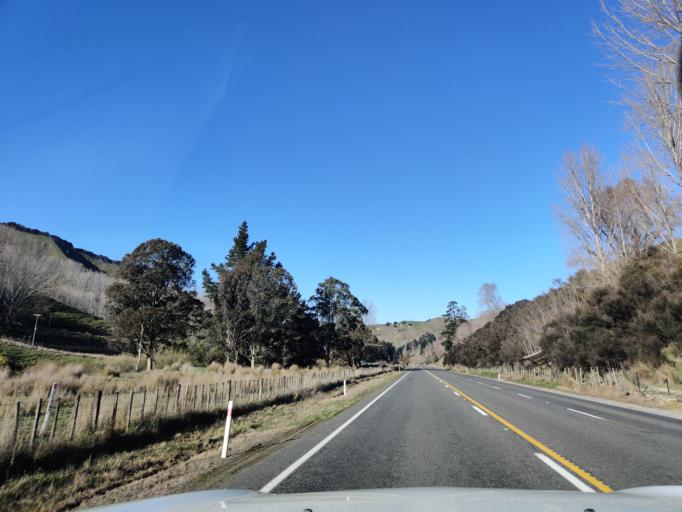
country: NZ
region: Manawatu-Wanganui
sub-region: Ruapehu District
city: Waiouru
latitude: -39.7824
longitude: 175.7863
